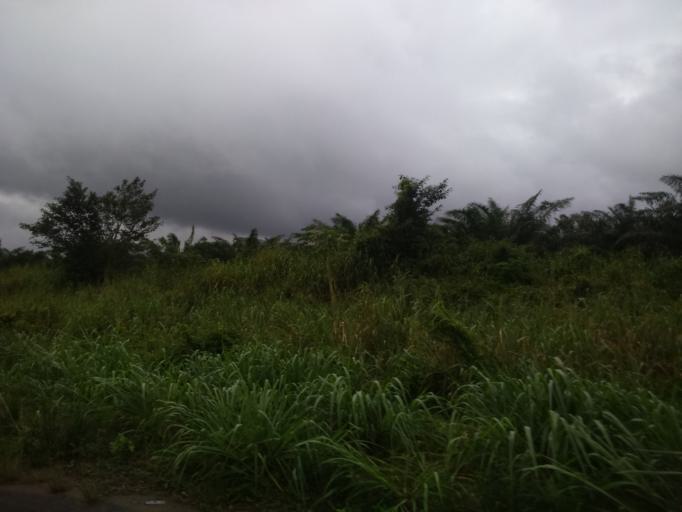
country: CI
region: Sud-Comoe
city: Adiake
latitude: 5.3007
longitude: -3.3513
